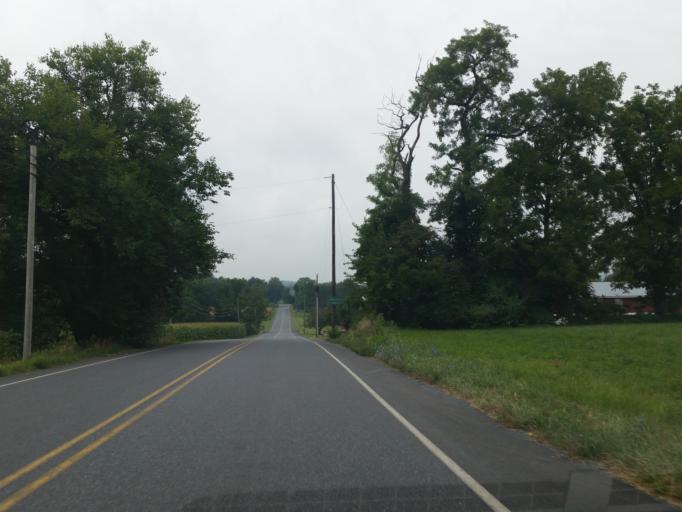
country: US
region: Pennsylvania
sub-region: Lancaster County
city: Brickerville
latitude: 40.2921
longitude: -76.2993
